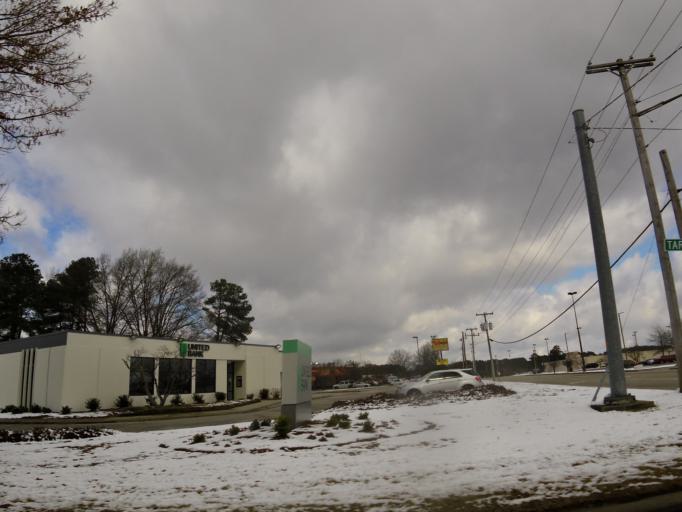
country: US
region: North Carolina
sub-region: Wilson County
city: Wilson
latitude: 35.7213
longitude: -77.9397
